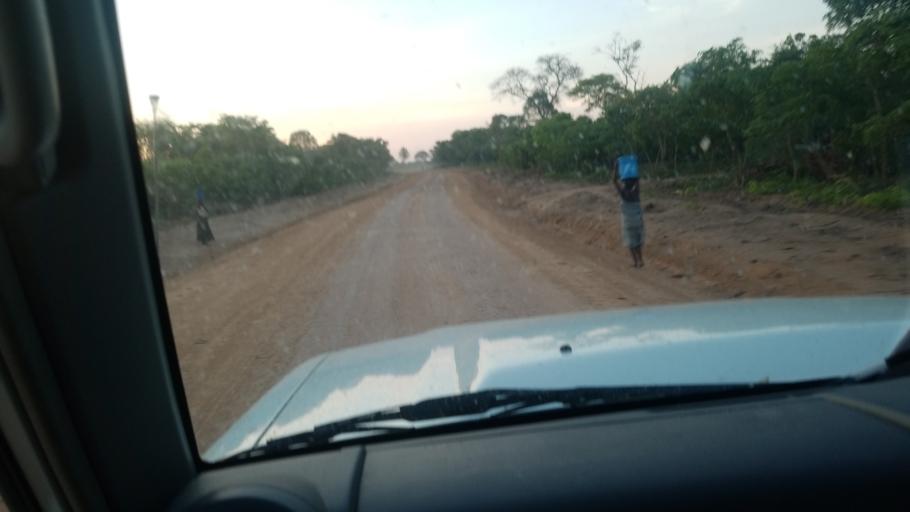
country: ZM
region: Northern
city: Luwingu
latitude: -10.5610
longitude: 29.9974
